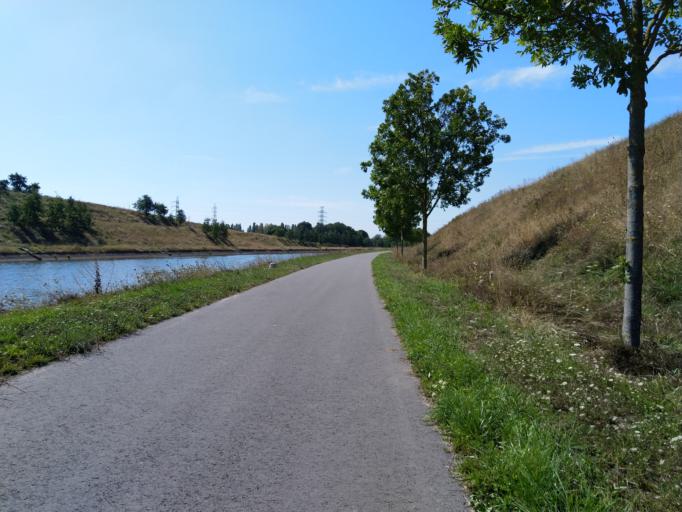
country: BE
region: Wallonia
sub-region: Province du Hainaut
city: Roeulx
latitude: 50.4714
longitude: 4.0802
